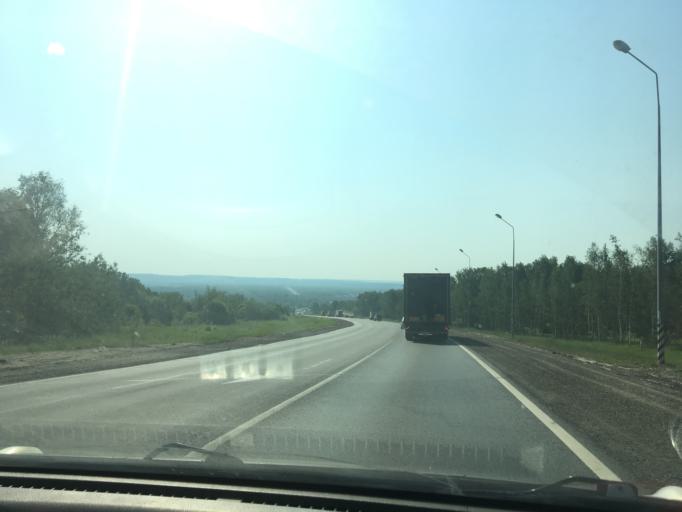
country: RU
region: Nizjnij Novgorod
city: Kstovo
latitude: 56.1062
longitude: 44.2891
